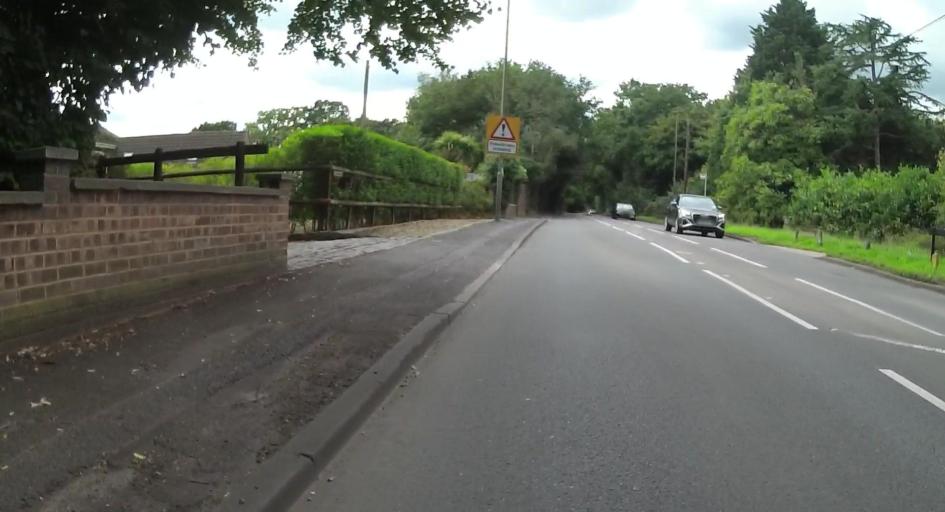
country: GB
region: England
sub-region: Surrey
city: Knaphill
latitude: 51.3261
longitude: -0.5983
